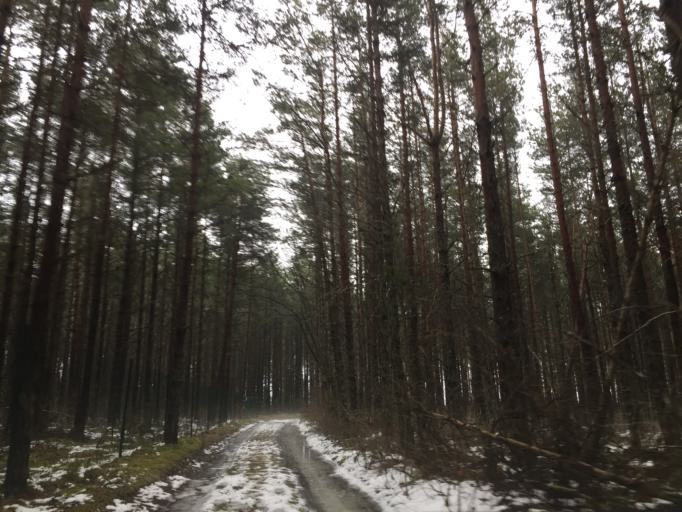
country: EE
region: Saare
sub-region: Orissaare vald
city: Orissaare
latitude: 58.6135
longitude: 22.9547
